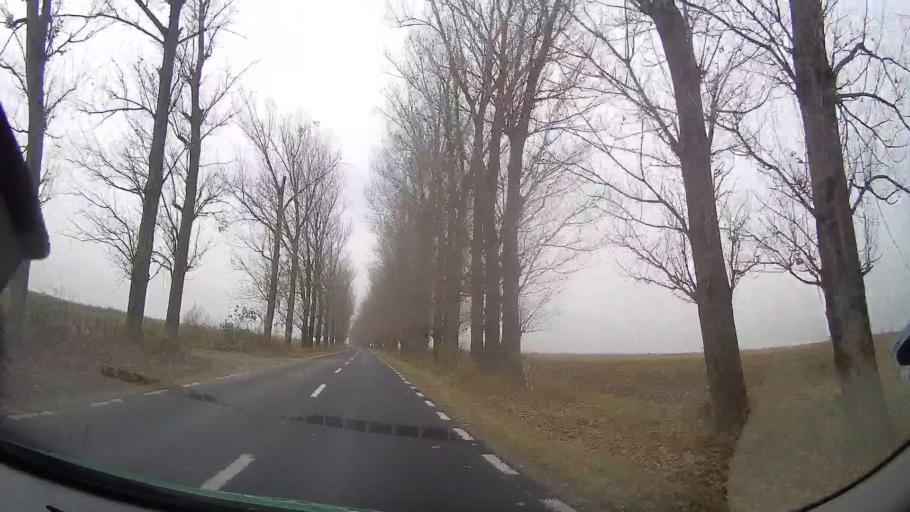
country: RO
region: Ilfov
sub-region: Comuna Nuci
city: Nuci
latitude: 44.7216
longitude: 26.2836
